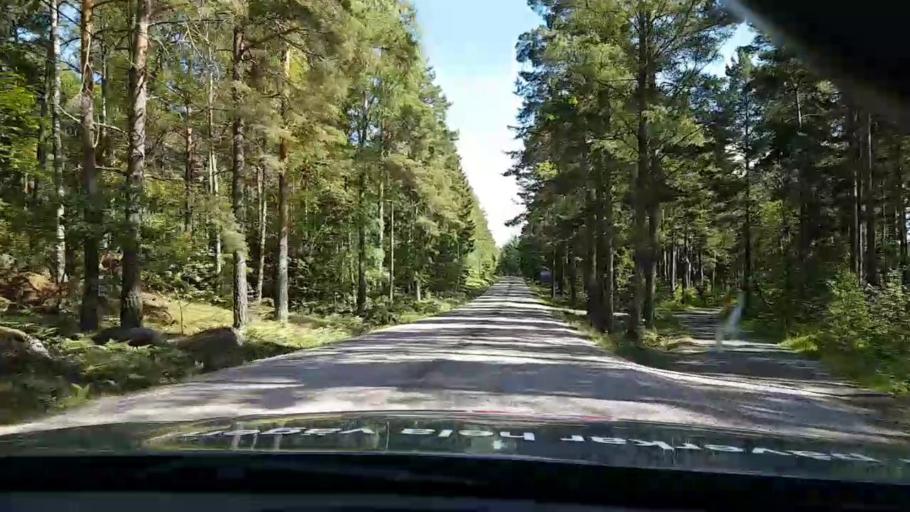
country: SE
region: Kalmar
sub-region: Vasterviks Kommun
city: Vaestervik
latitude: 57.9120
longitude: 16.6414
